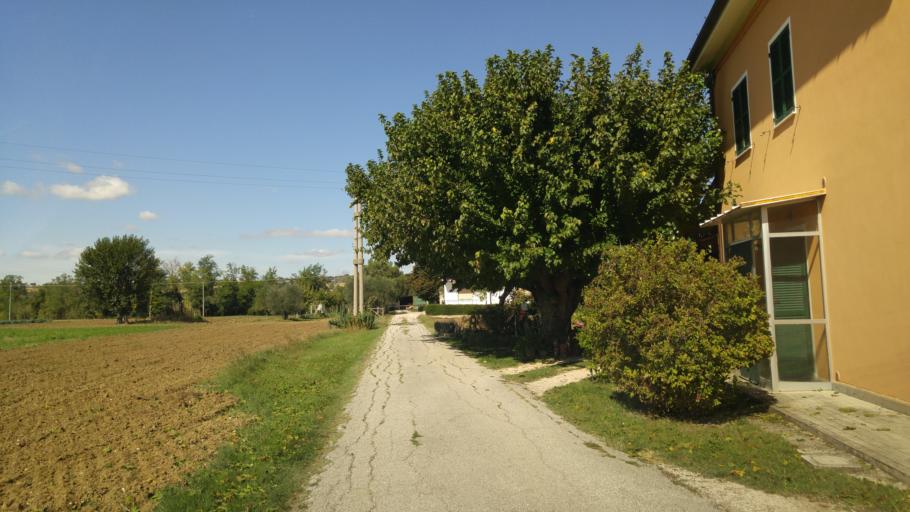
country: IT
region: The Marches
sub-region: Provincia di Pesaro e Urbino
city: Cuccurano
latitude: 43.7782
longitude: 12.9564
